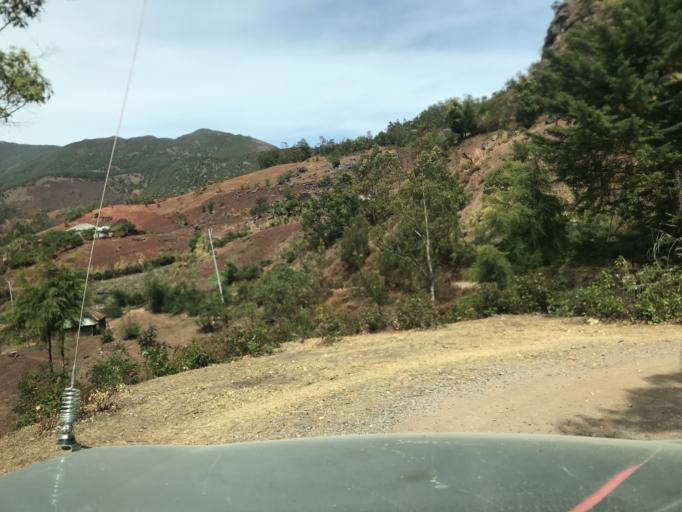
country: TL
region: Ainaro
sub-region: Ainaro
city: Ainaro
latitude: -8.8839
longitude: 125.5233
